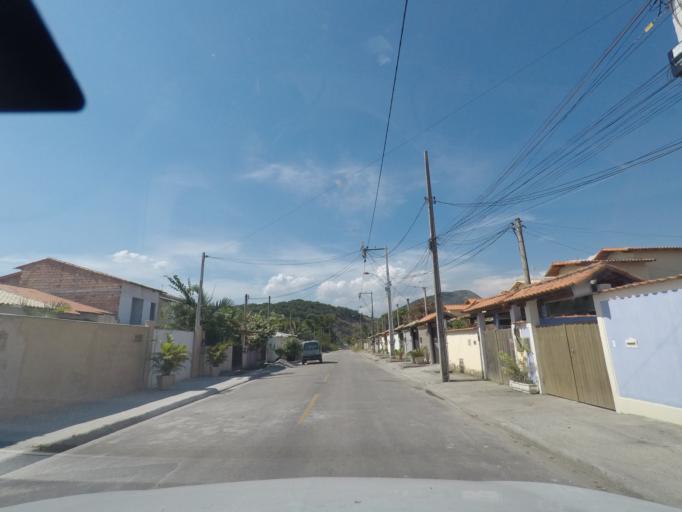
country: BR
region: Rio de Janeiro
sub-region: Niteroi
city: Niteroi
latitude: -22.9609
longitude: -42.9703
